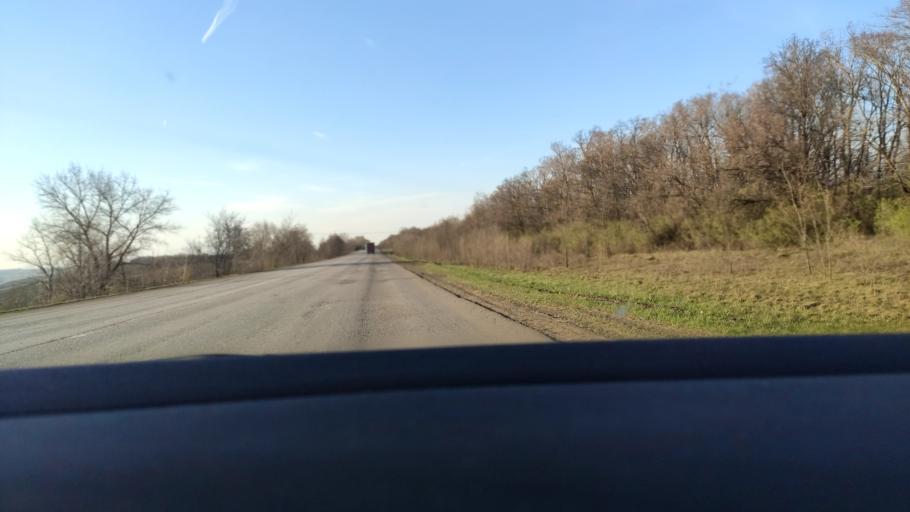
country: RU
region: Voronezj
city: Uryv-Pokrovka
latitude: 51.2348
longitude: 39.0586
